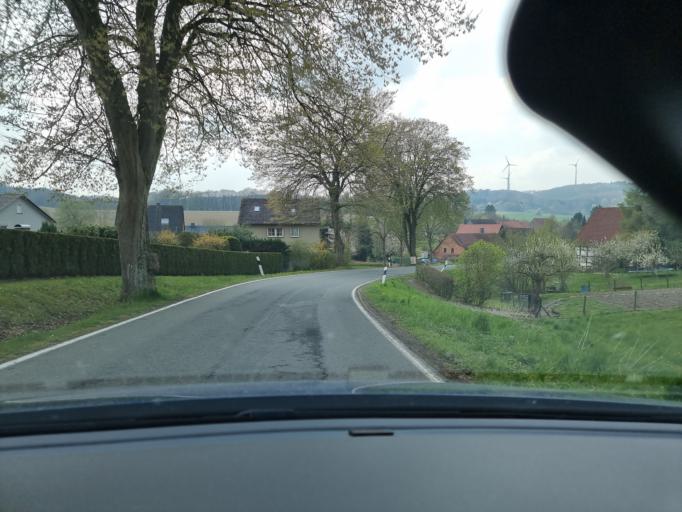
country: DE
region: North Rhine-Westphalia
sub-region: Regierungsbezirk Detmold
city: Dorentrup
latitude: 52.1209
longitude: 9.0102
